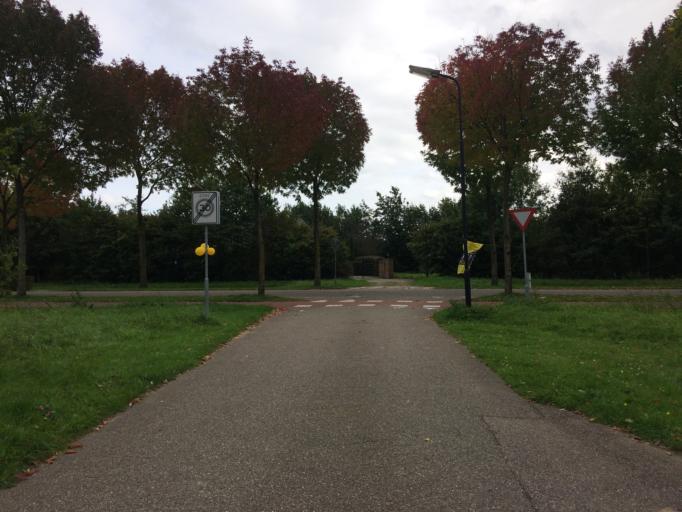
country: NL
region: Gelderland
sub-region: Gemeente Maasdriel
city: Hedel
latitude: 51.7192
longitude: 5.2577
